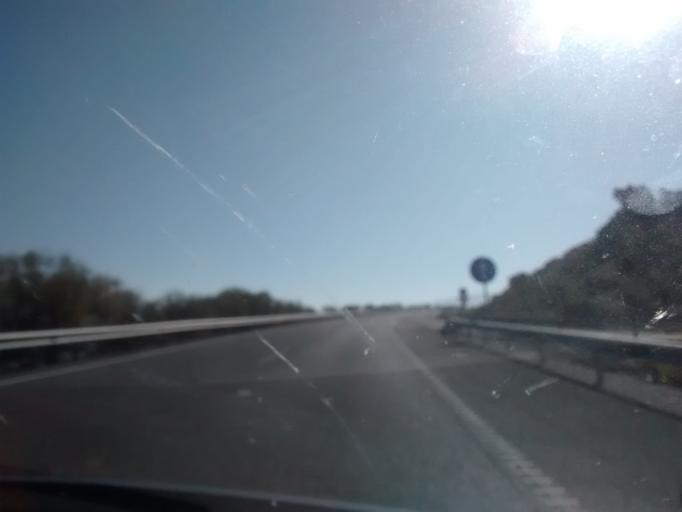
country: ES
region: Andalusia
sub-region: Provincia de Cadiz
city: Paterna de Rivera
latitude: 36.4716
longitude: -5.8051
